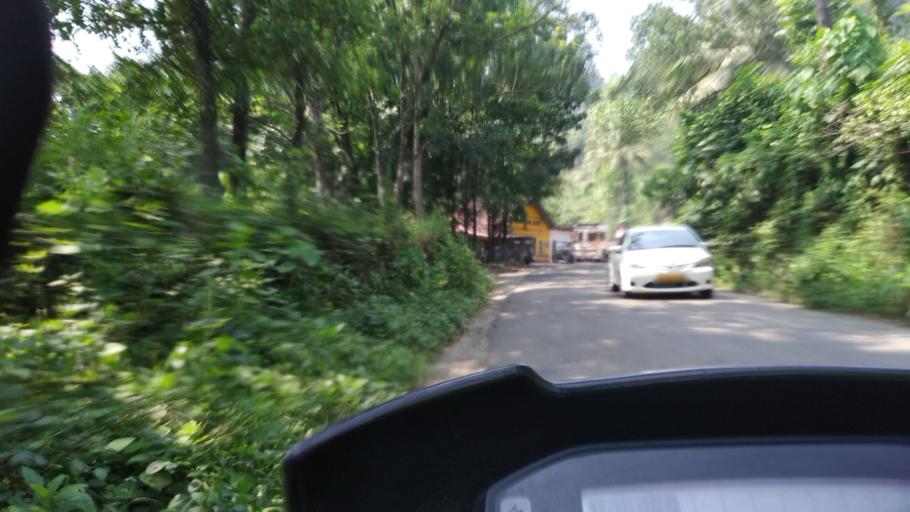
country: IN
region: Kerala
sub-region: Kottayam
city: Erattupetta
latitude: 9.6887
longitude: 76.8269
